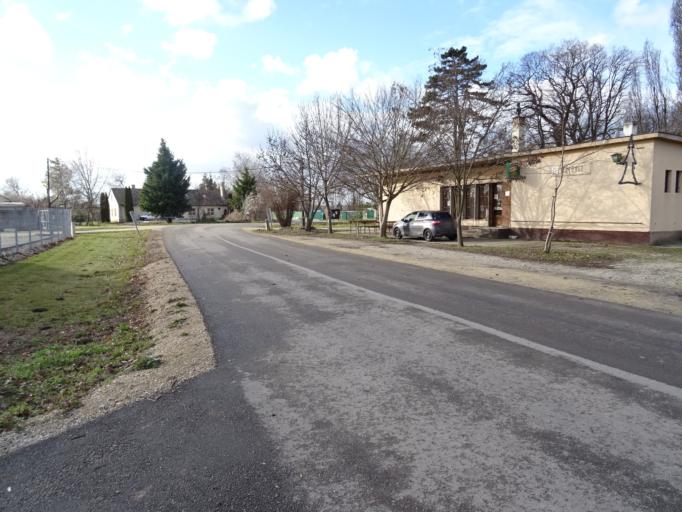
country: HU
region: Gyor-Moson-Sopron
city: Kimle
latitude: 47.8011
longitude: 17.3468
